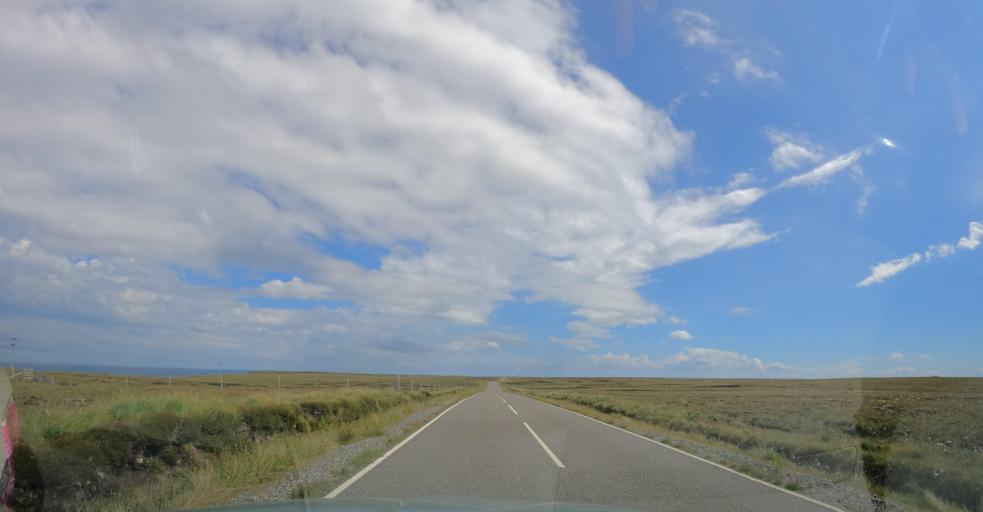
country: GB
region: Scotland
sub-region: Eilean Siar
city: Isle of Lewis
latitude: 58.4527
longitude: -6.3475
